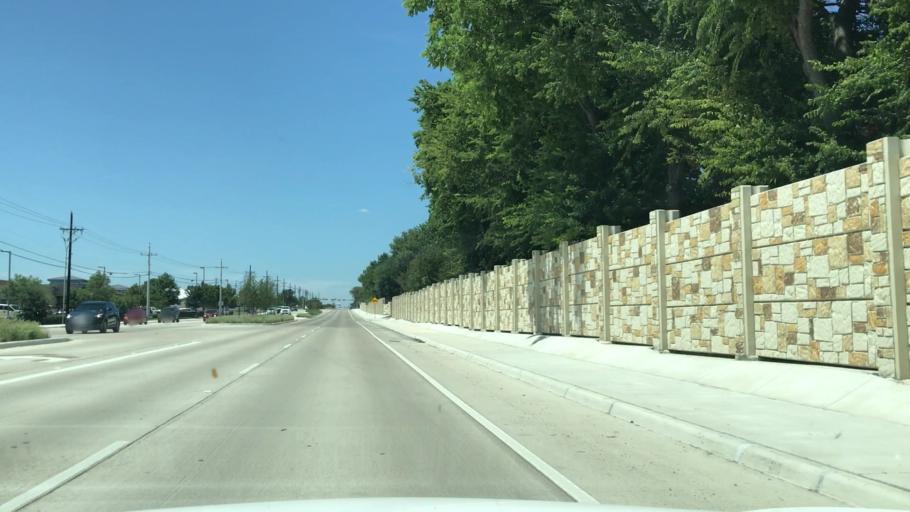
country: US
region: Texas
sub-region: Rockwall County
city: Rockwall
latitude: 32.8859
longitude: -96.4643
